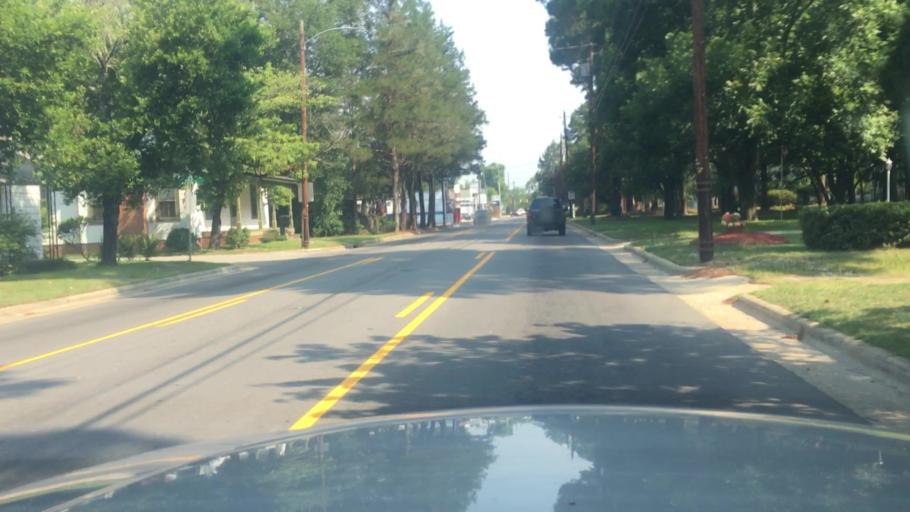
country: US
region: North Carolina
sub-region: Cumberland County
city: Hope Mills
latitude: 34.9689
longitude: -78.9450
